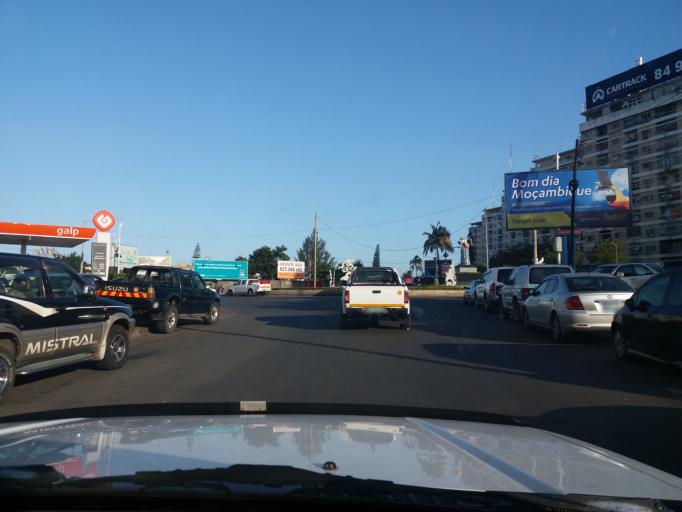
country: MZ
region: Maputo City
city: Maputo
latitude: -25.9524
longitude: 32.5882
